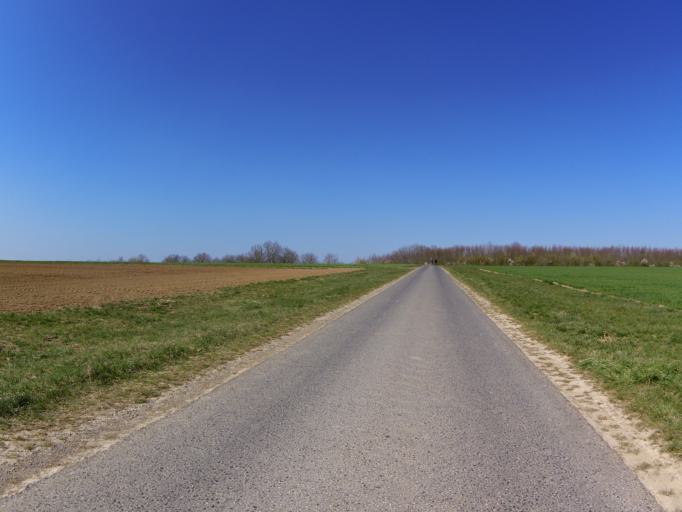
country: DE
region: Bavaria
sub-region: Regierungsbezirk Unterfranken
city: Kurnach
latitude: 49.8377
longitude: 10.0621
